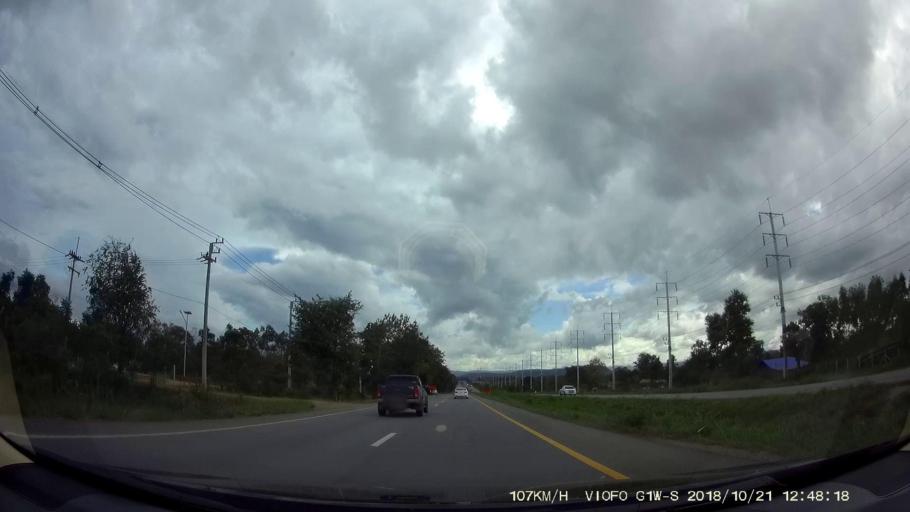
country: TH
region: Nakhon Ratchasima
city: Amphoe Sikhiu
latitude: 14.9147
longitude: 101.6840
